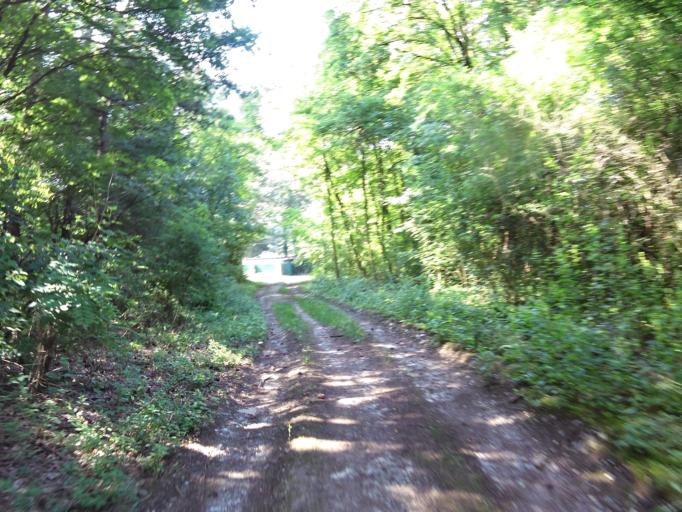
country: DE
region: Bavaria
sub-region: Regierungsbezirk Unterfranken
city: Hochberg
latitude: 49.7757
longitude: 9.9095
